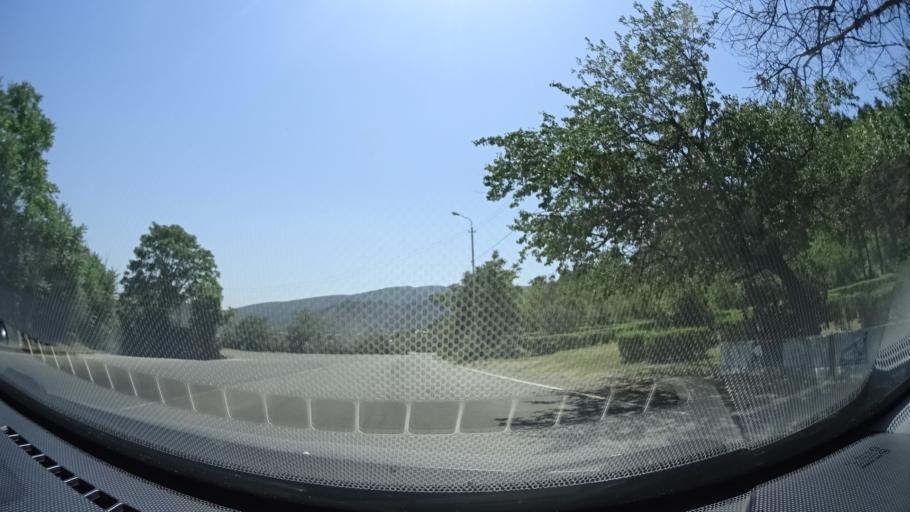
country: GE
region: Mtskheta-Mtianeti
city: Mtskheta
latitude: 41.8552
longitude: 44.7218
